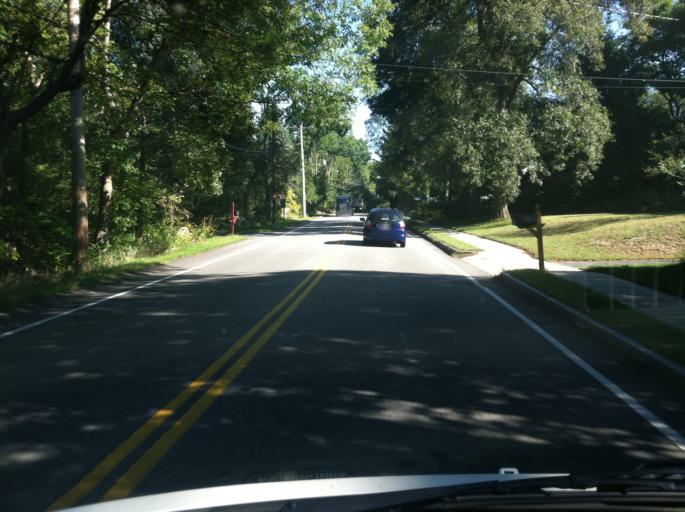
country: US
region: Massachusetts
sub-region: Middlesex County
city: Bedford
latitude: 42.4898
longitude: -71.2913
